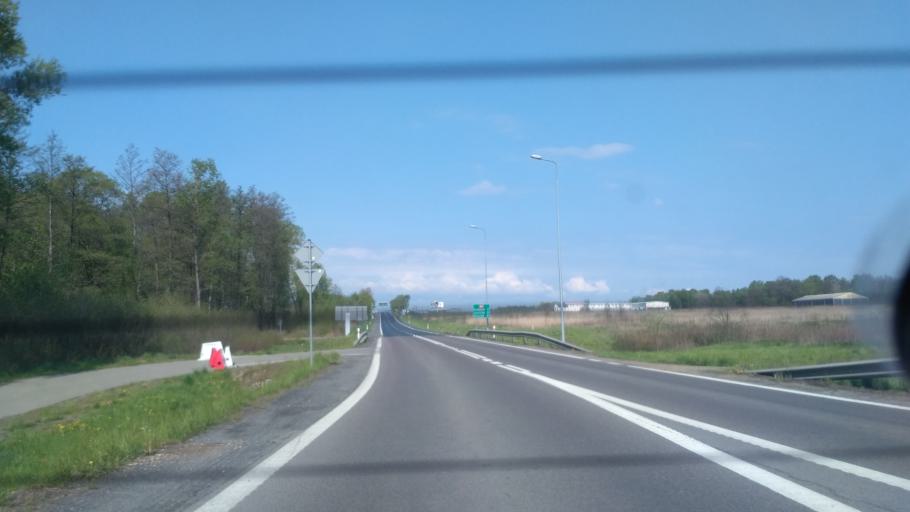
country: PL
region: Subcarpathian Voivodeship
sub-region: Powiat lubaczowski
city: Wielkie Oczy
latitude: 49.9671
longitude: 23.0661
